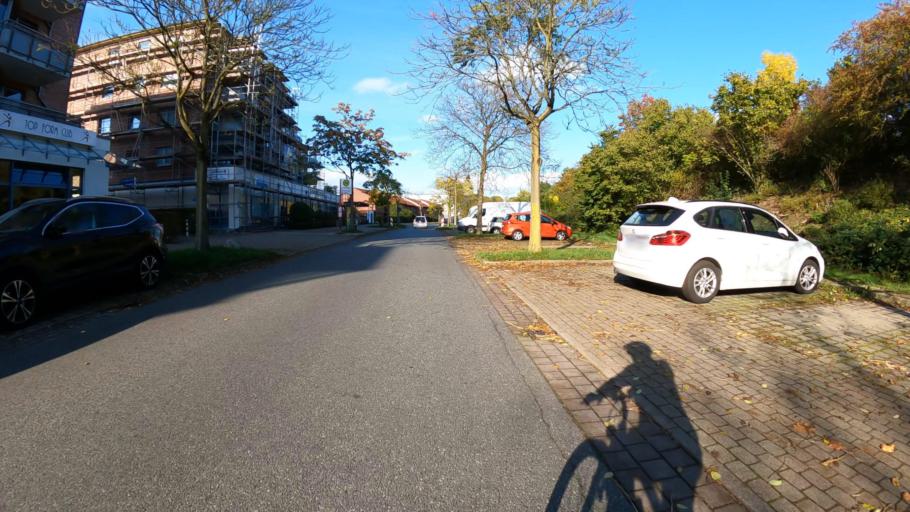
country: DE
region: Schleswig-Holstein
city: Delingsdorf
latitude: 53.6832
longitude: 10.2488
